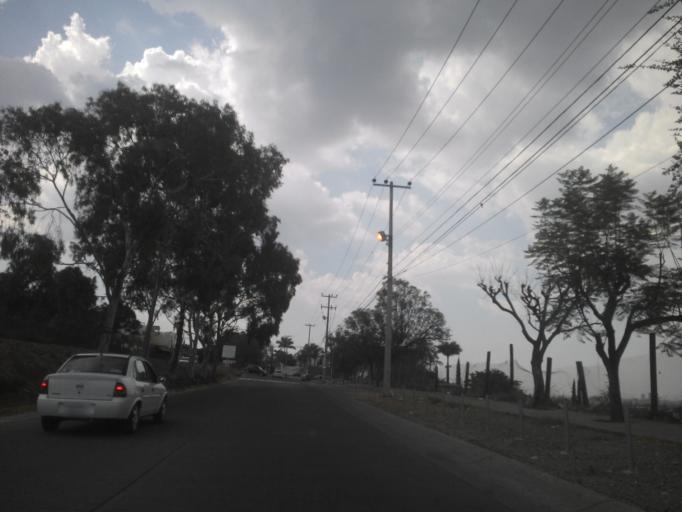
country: MX
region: Jalisco
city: Guadalajara
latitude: 20.6161
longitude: -103.4018
